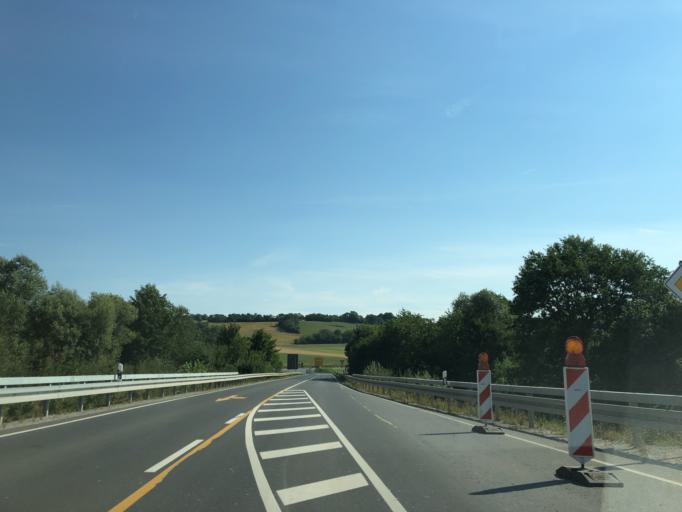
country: DE
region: Bavaria
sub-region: Regierungsbezirk Unterfranken
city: Geiselwind
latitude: 49.7710
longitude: 10.4768
